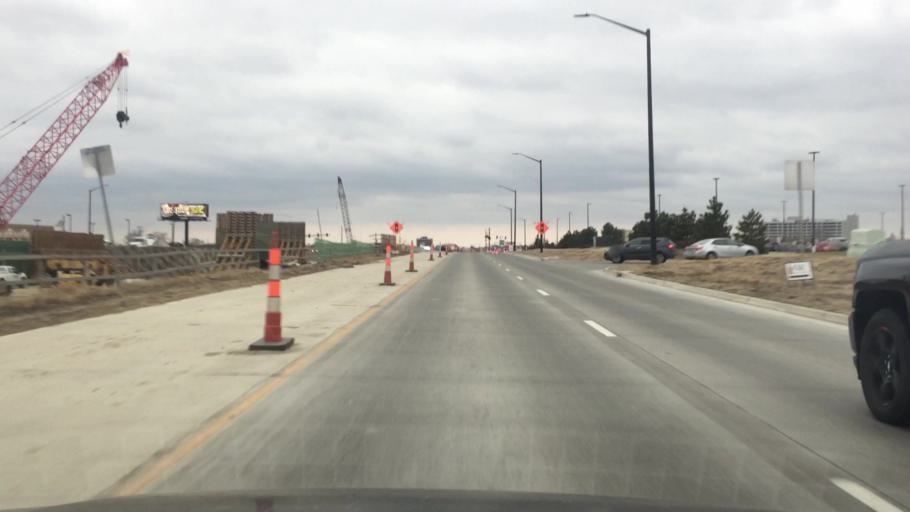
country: US
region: Kansas
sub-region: Butler County
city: Andover
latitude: 37.6794
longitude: -97.2219
